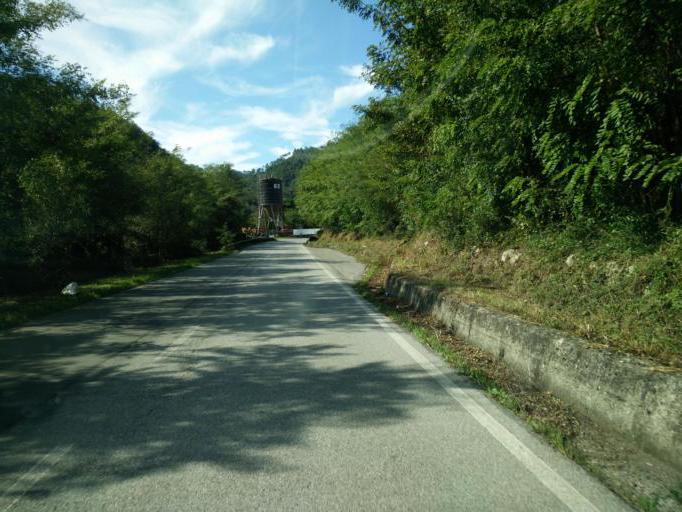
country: IT
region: Liguria
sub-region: Provincia di La Spezia
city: Carrodano
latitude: 44.2690
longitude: 9.6586
